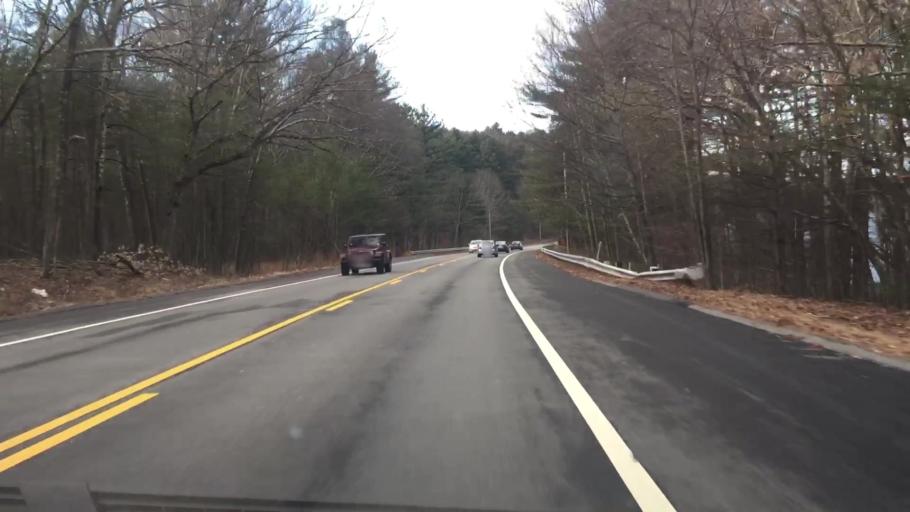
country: US
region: Massachusetts
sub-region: Worcester County
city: West Boylston
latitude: 42.3390
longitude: -71.7530
